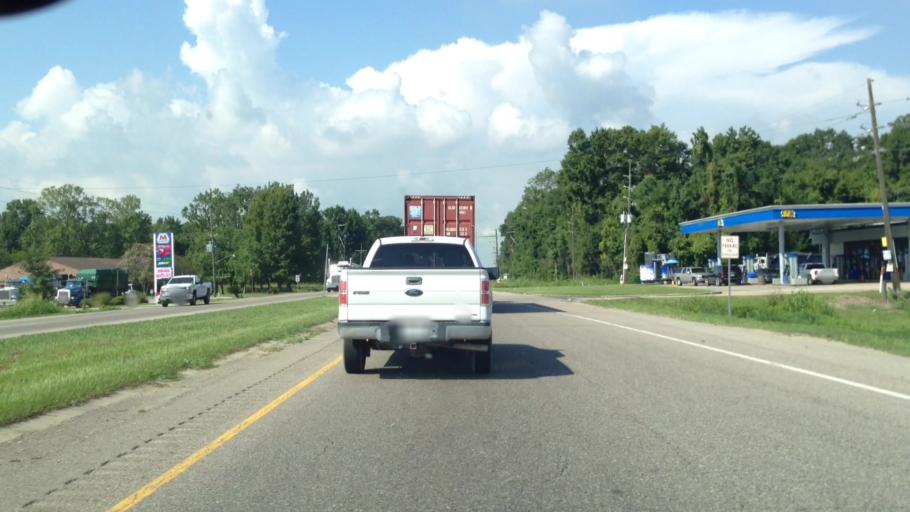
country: US
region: Louisiana
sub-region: Ascension Parish
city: Sorrento
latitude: 30.1705
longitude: -90.8780
